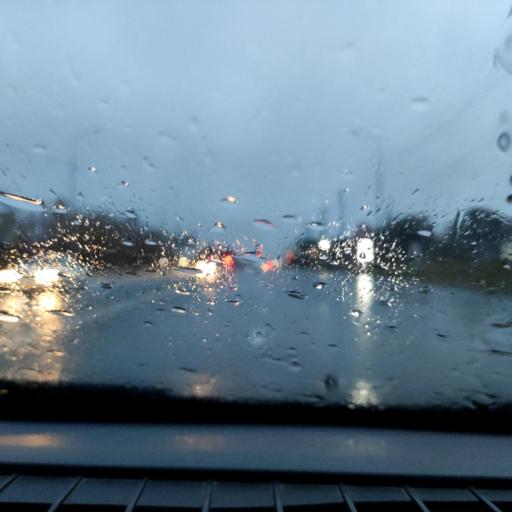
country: RU
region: Samara
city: Tol'yatti
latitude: 53.5677
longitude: 49.2912
